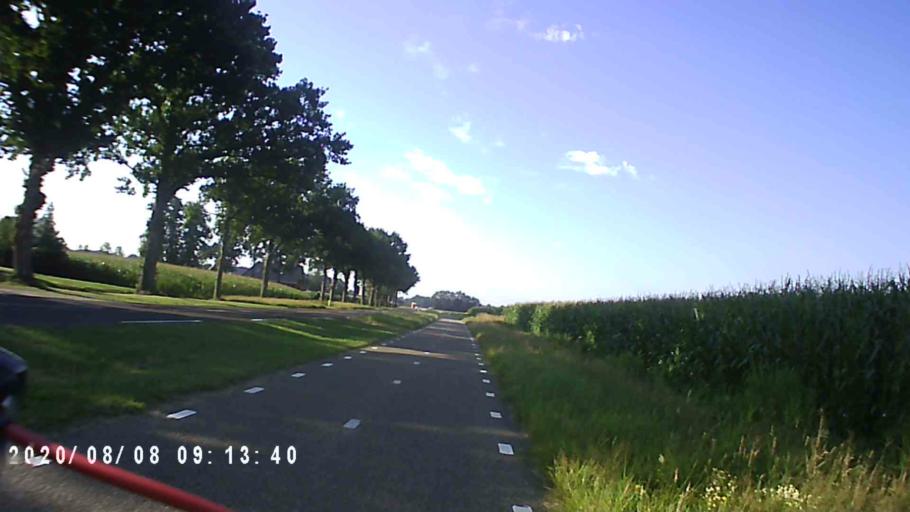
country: NL
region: Groningen
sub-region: Gemeente Leek
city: Leek
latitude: 53.0504
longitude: 6.3315
